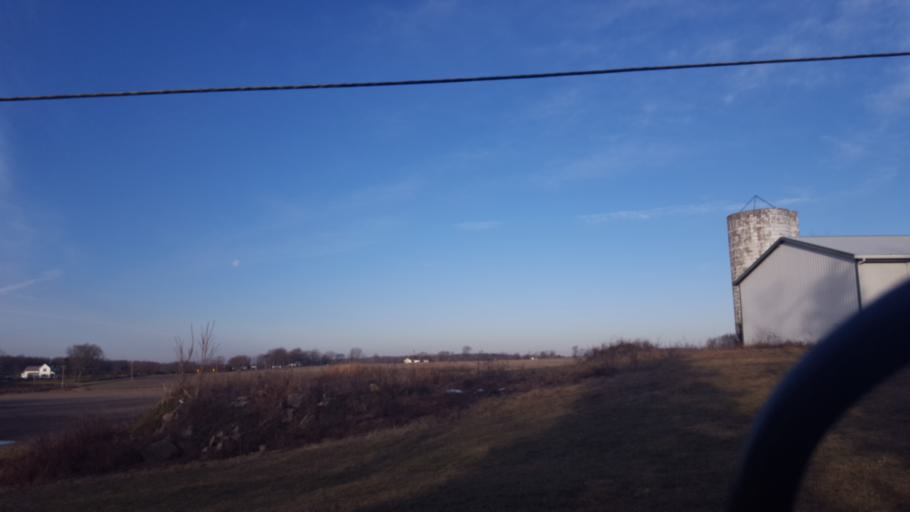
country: US
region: Ohio
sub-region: Morrow County
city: Cardington
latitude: 40.4837
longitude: -82.8389
